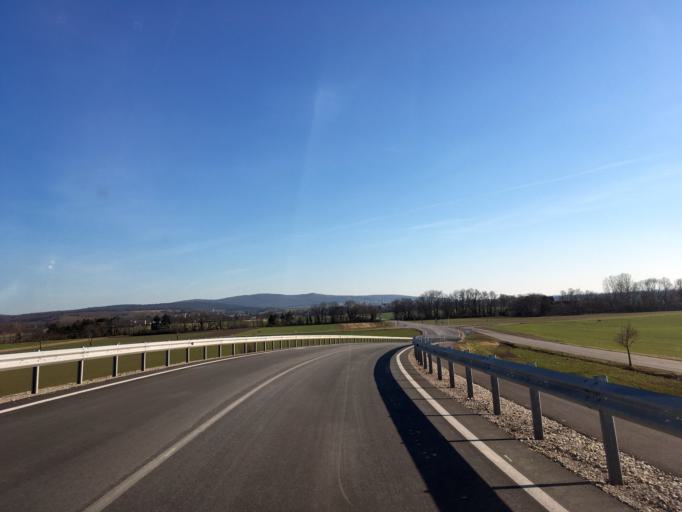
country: AT
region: Burgenland
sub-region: Eisenstadt-Umgebung
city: Wimpassing an der Leitha
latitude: 47.9346
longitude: 16.4197
